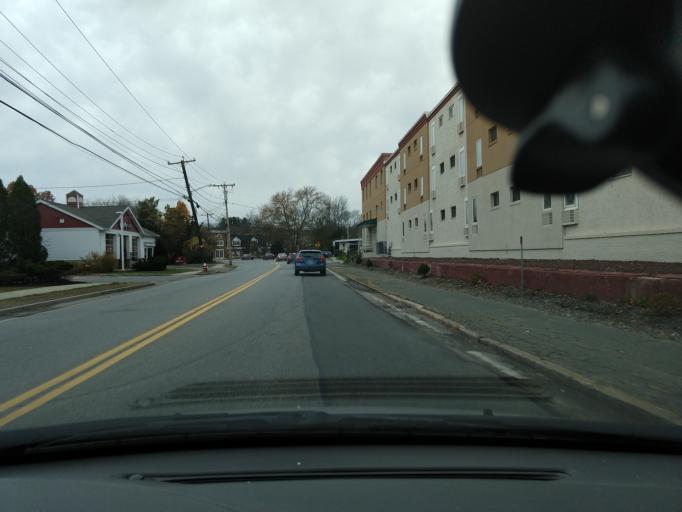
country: US
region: Massachusetts
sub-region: Middlesex County
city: Bedford
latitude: 42.4853
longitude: -71.2607
